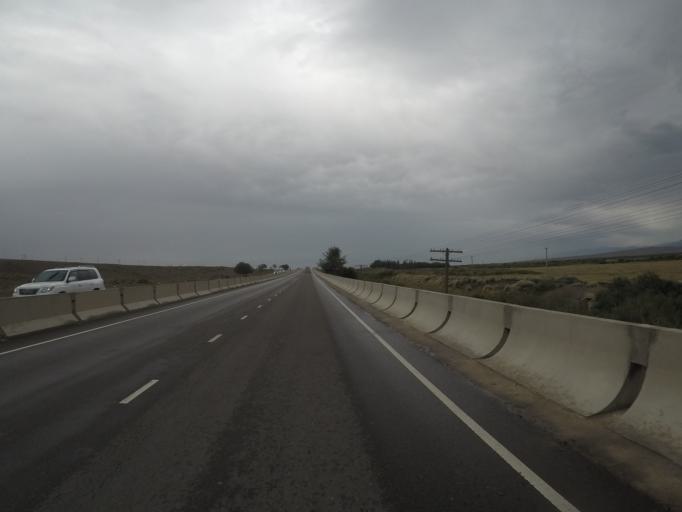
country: KG
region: Ysyk-Koel
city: Balykchy
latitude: 42.4617
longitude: 76.0593
